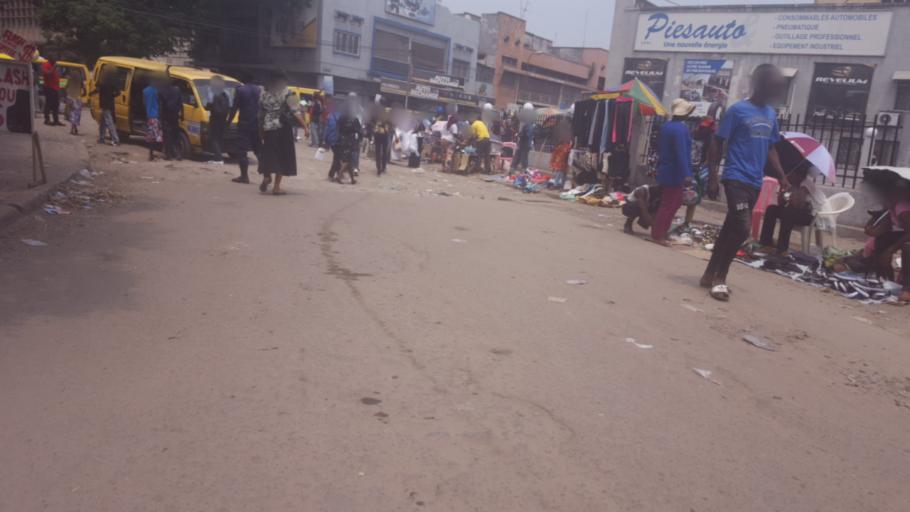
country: CD
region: Kinshasa
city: Kinshasa
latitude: -4.3073
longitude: 15.3088
